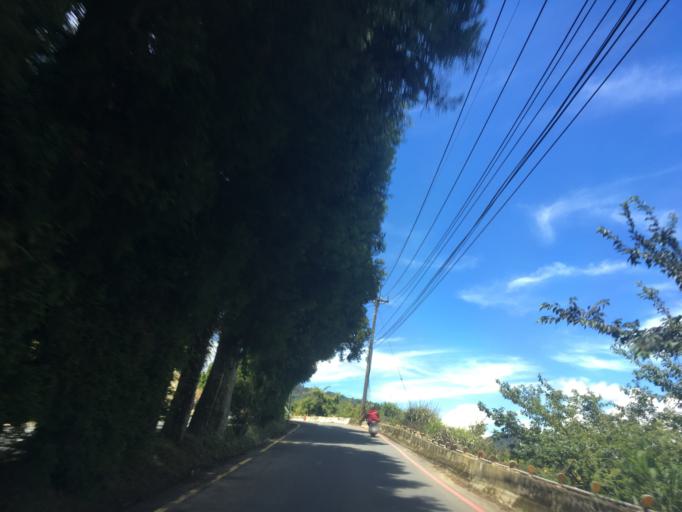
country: TW
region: Taiwan
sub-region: Nantou
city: Puli
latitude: 24.2464
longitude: 121.2422
